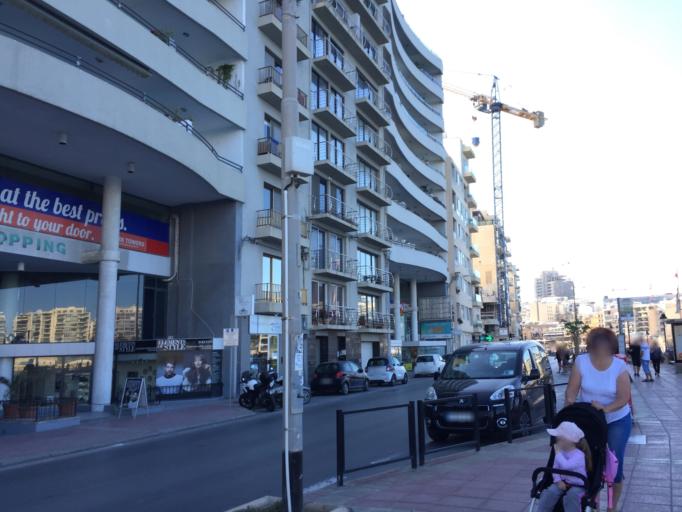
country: MT
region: Saint Julian
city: San Giljan
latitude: 35.9169
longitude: 14.4937
